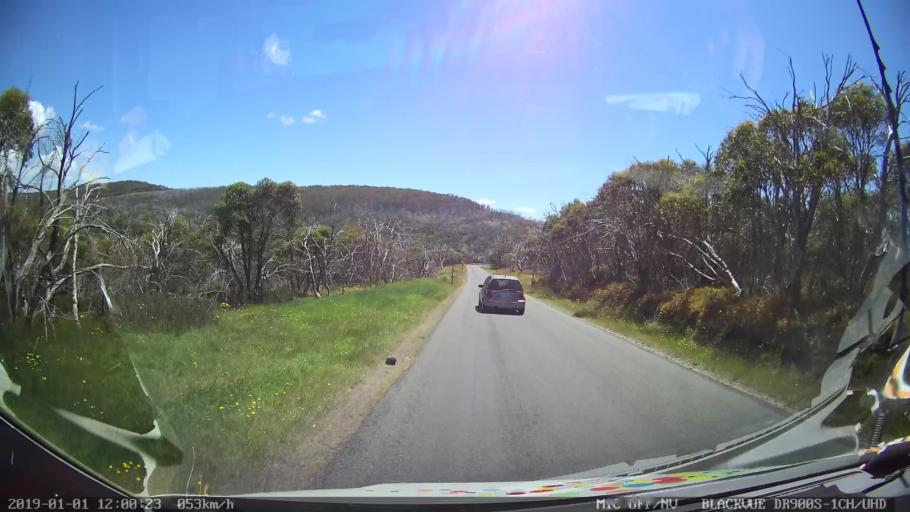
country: AU
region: New South Wales
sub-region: Snowy River
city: Jindabyne
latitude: -35.8852
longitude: 148.4592
